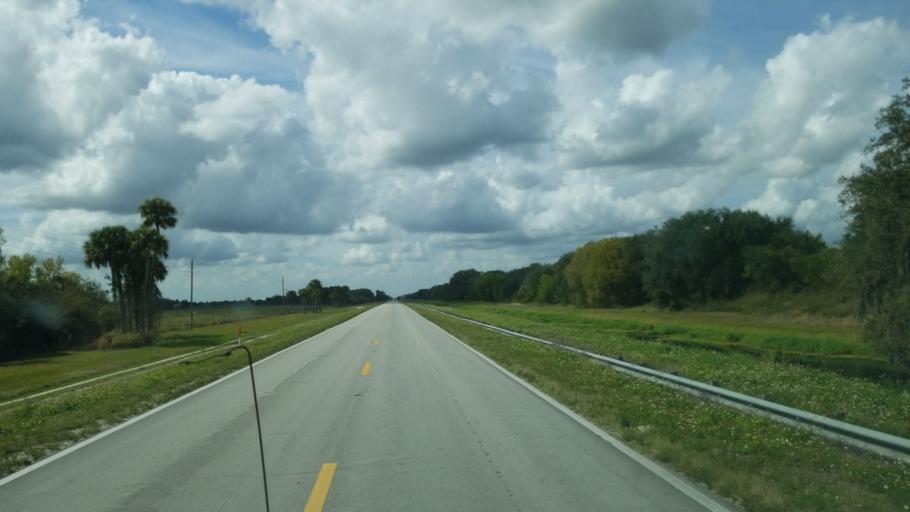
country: US
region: Florida
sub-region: Saint Lucie County
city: Lakewood Park
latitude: 27.4482
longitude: -80.5958
